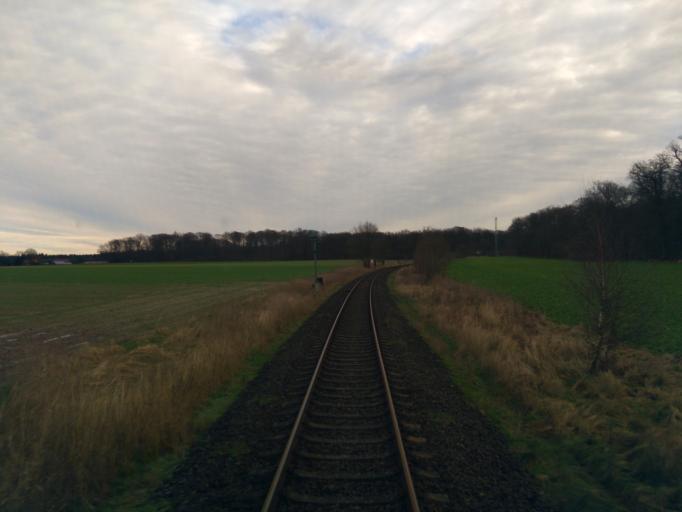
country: DE
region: Lower Saxony
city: Schwienau
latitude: 53.0201
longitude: 10.4372
